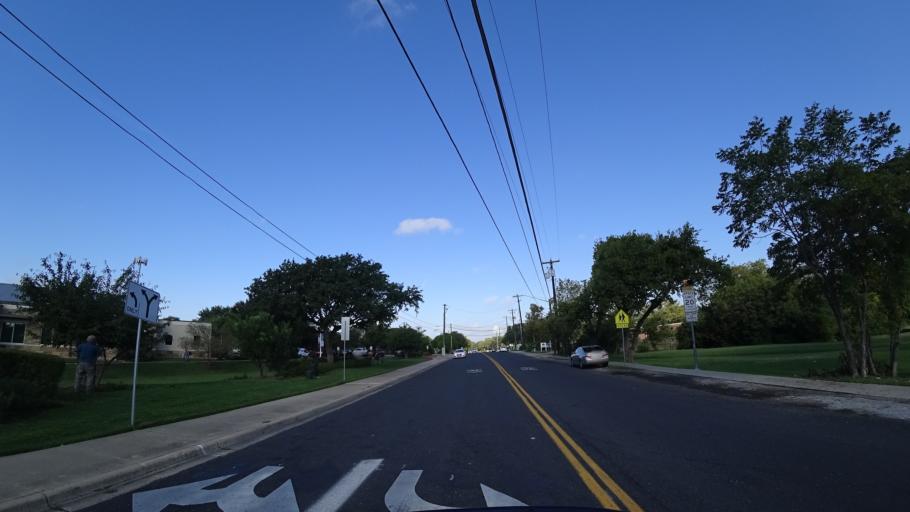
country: US
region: Texas
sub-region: Travis County
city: Rollingwood
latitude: 30.2089
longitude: -97.8052
